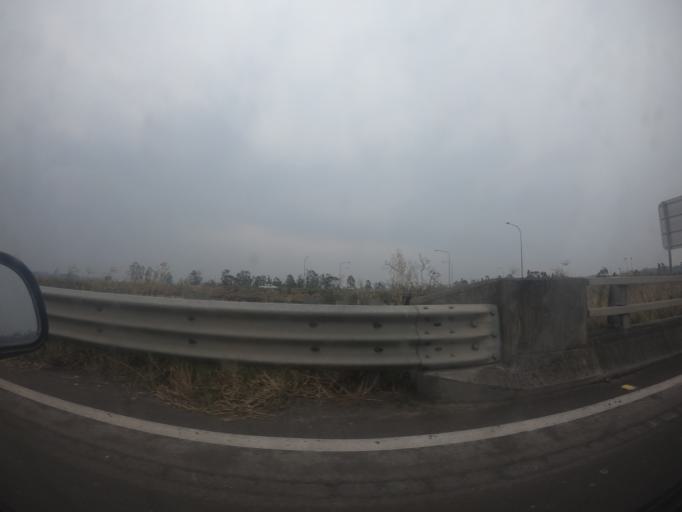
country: AU
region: New South Wales
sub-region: Shellharbour
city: Albion Park Rail
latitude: -34.5745
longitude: 150.8211
